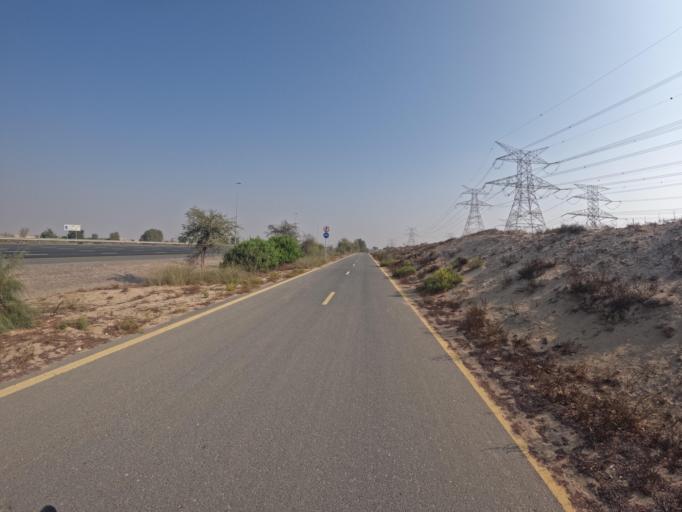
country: AE
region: Dubai
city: Dubai
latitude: 25.0455
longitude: 55.3056
